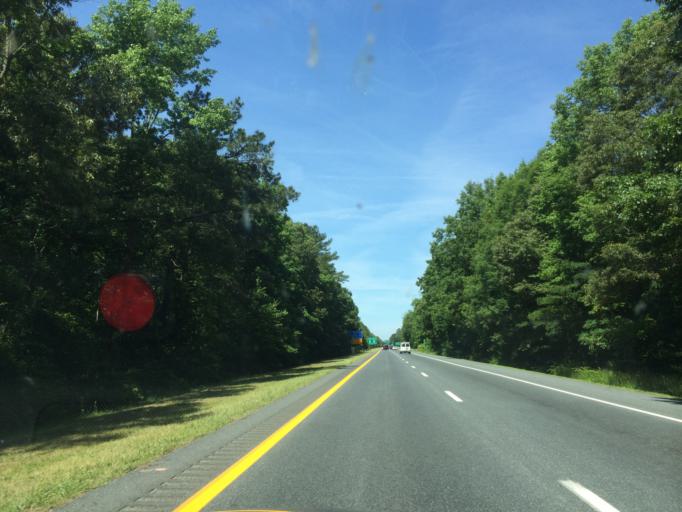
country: US
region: Maryland
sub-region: Wicomico County
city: Salisbury
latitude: 38.3751
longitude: -75.5066
